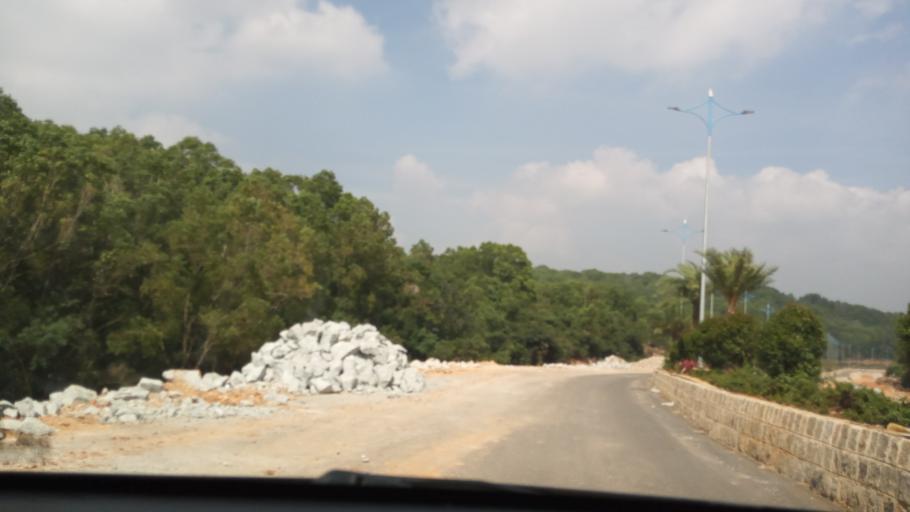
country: IN
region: Andhra Pradesh
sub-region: Chittoor
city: Tirumala
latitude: 13.6887
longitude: 79.3431
